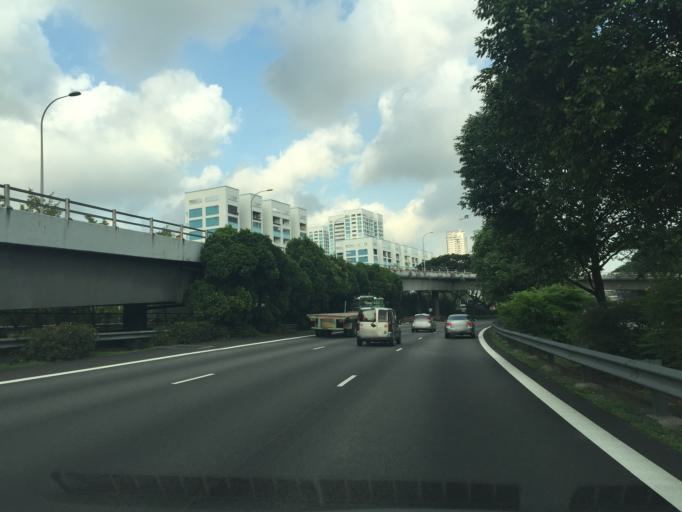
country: SG
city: Singapore
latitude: 1.3293
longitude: 103.8573
